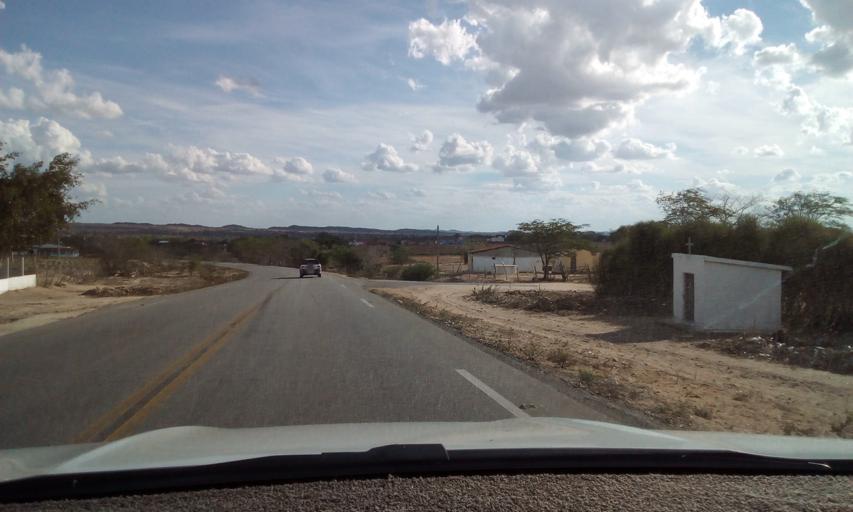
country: BR
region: Paraiba
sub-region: Soledade
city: Soledade
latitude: -6.9308
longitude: -36.3864
